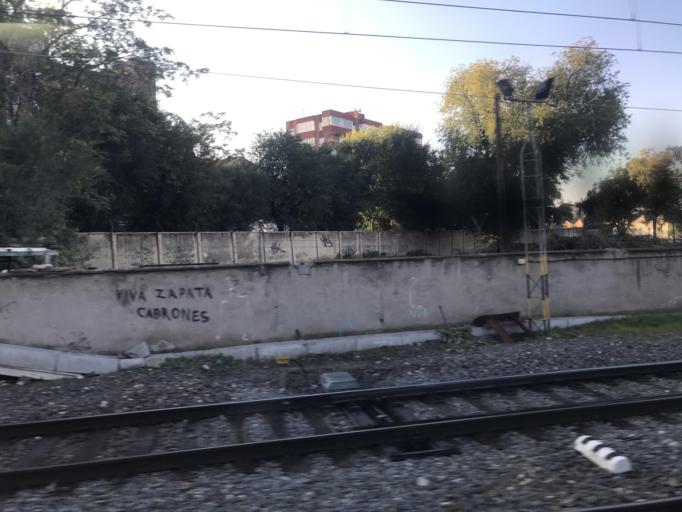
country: ES
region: Castille and Leon
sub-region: Provincia de Valladolid
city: Valladolid
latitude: 41.6439
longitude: -4.7215
